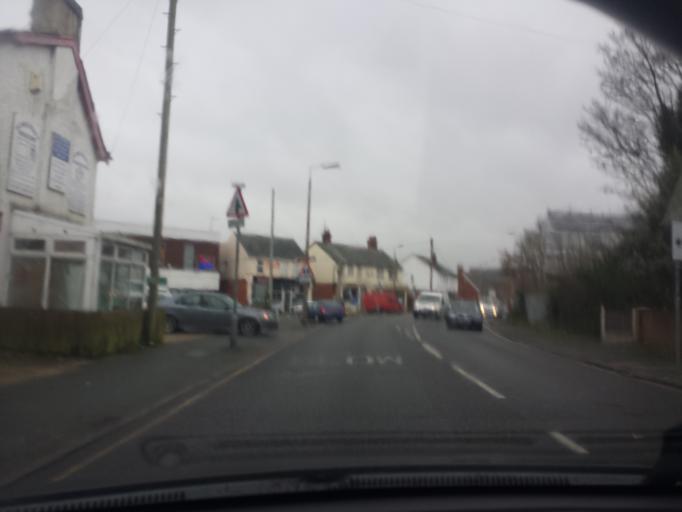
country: GB
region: England
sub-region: Essex
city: Dovercourt
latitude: 51.9338
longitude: 1.2584
